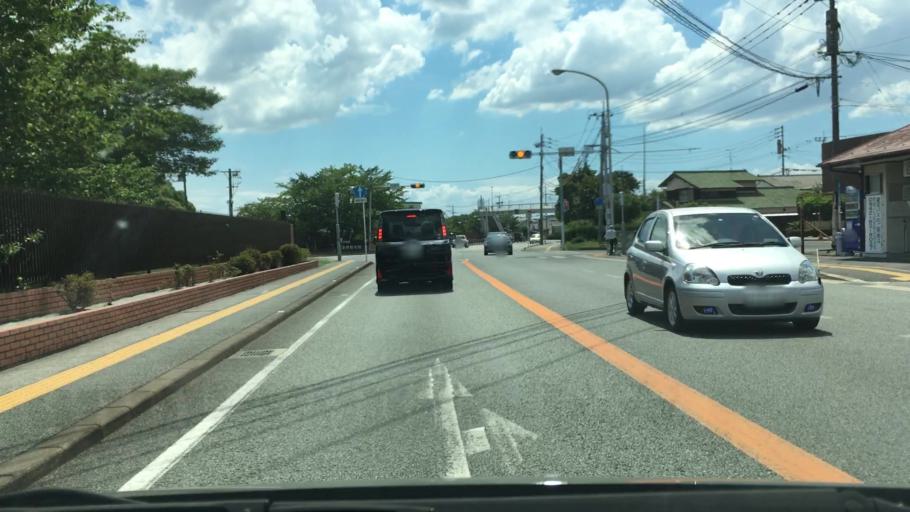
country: JP
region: Saga Prefecture
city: Kanzakimachi-kanzaki
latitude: 33.3277
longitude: 130.4094
